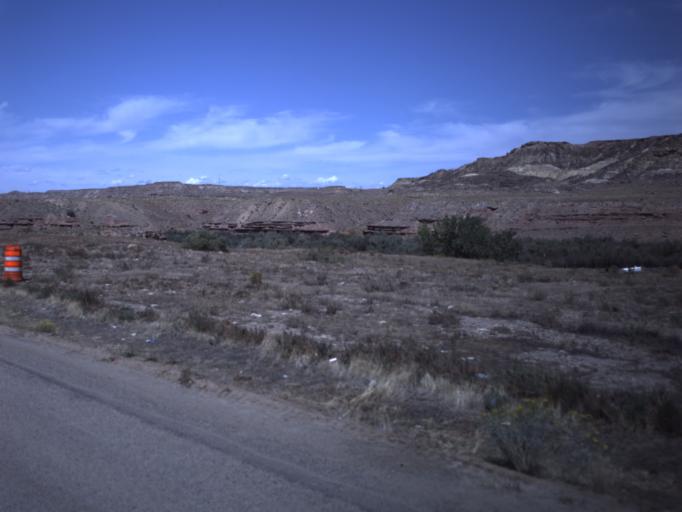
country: US
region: Colorado
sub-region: Montezuma County
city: Towaoc
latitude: 37.2161
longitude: -109.1863
